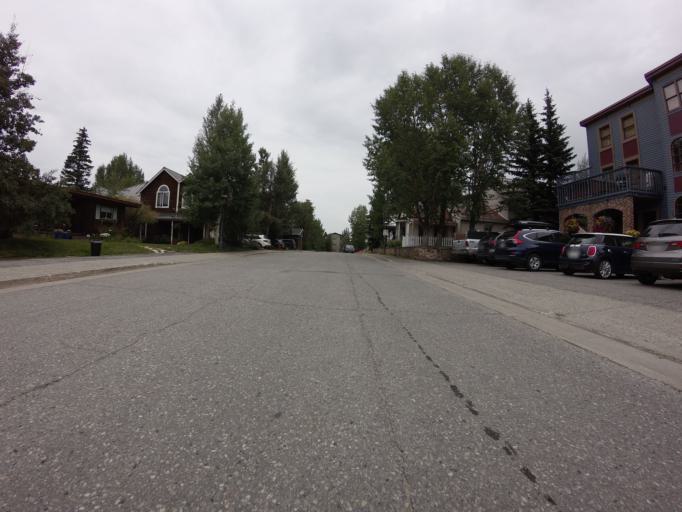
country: US
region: Colorado
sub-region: Summit County
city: Breckenridge
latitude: 39.4836
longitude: -106.0449
